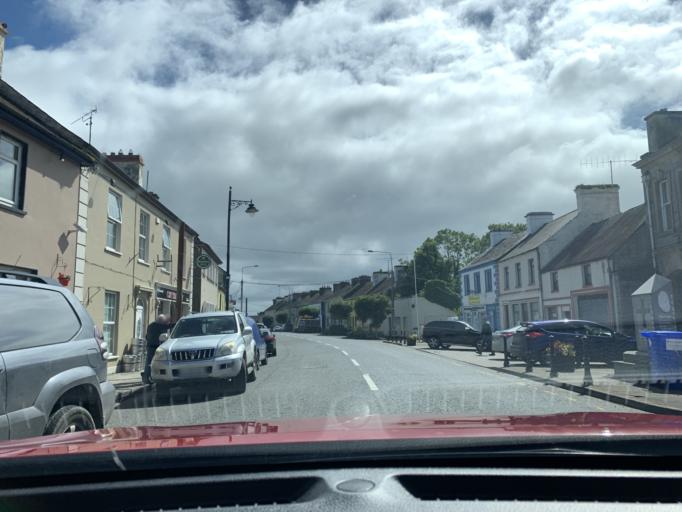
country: IE
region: Connaught
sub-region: County Leitrim
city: Carrick-on-Shannon
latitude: 53.8458
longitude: -8.1948
